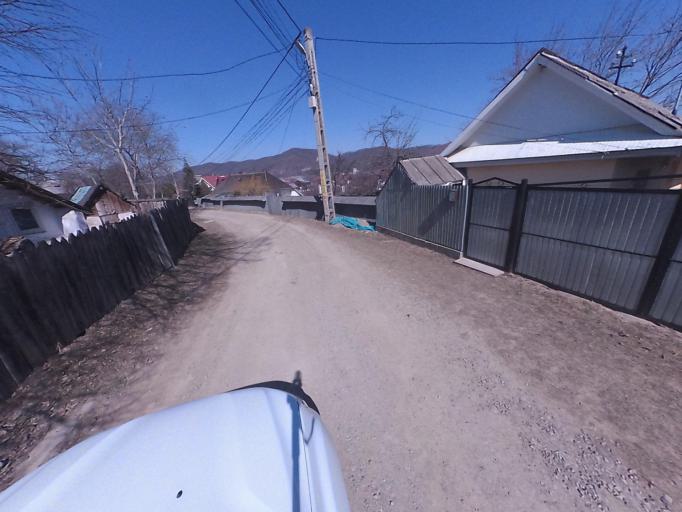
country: RO
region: Neamt
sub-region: Oras Targu Neamt
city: Humulesti
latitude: 47.1989
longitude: 26.3402
